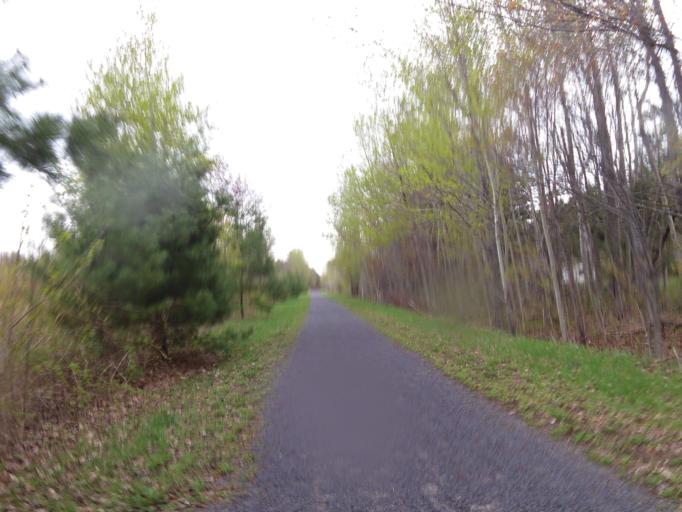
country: CA
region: Ontario
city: Bourget
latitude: 45.4429
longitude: -75.1416
